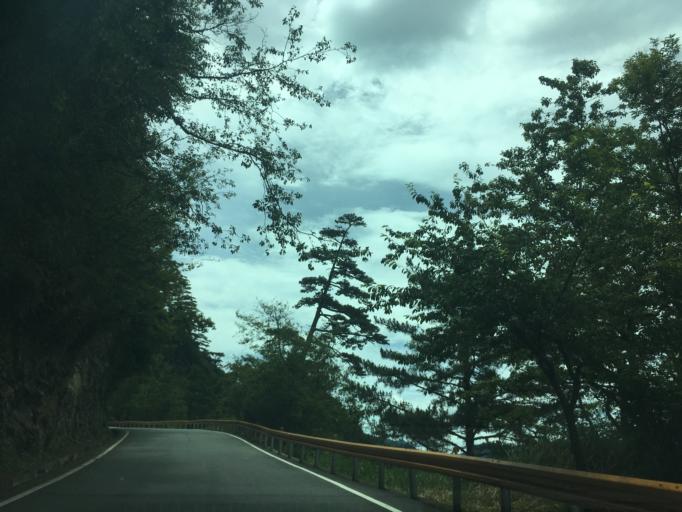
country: TW
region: Taiwan
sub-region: Hualien
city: Hualian
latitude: 24.1806
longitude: 121.3570
